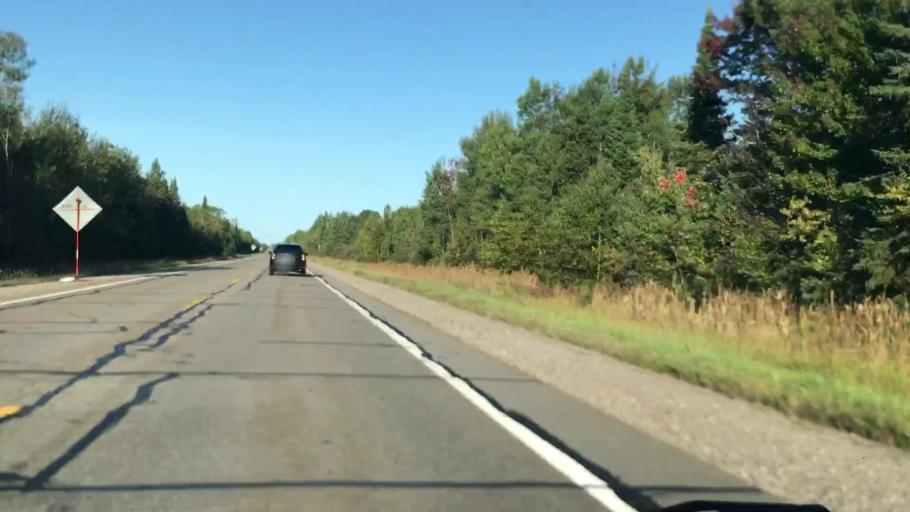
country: US
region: Michigan
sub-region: Chippewa County
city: Sault Ste. Marie
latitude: 46.3758
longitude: -84.6307
